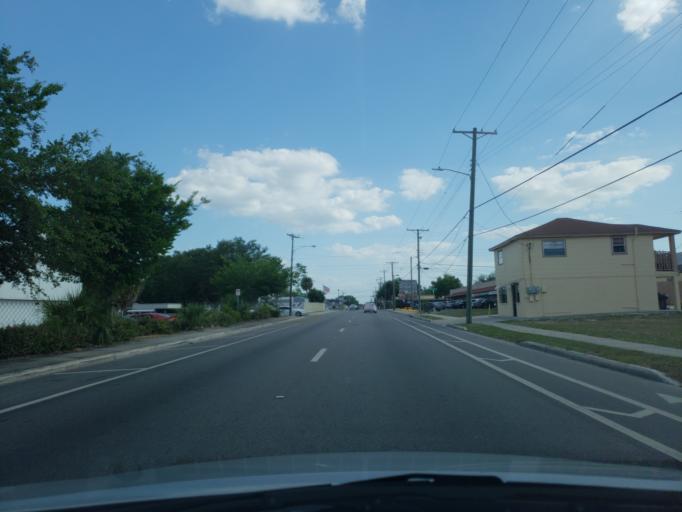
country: US
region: Florida
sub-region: Hillsborough County
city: Tampa
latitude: 27.9725
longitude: -82.4848
